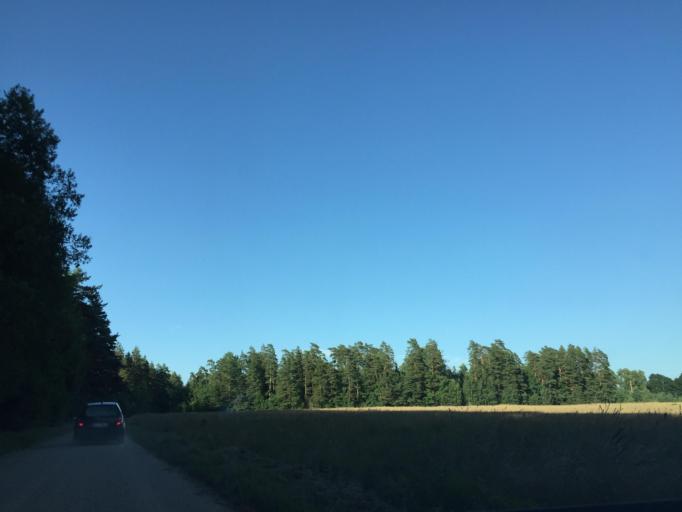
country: LV
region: Kandava
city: Kandava
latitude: 57.0171
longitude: 22.7465
